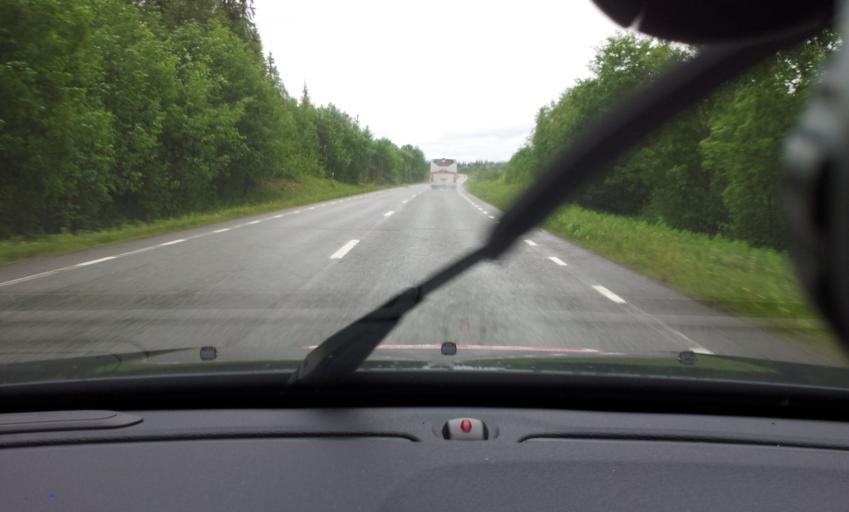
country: SE
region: Jaemtland
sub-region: Krokoms Kommun
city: Krokom
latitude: 63.5642
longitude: 14.6121
